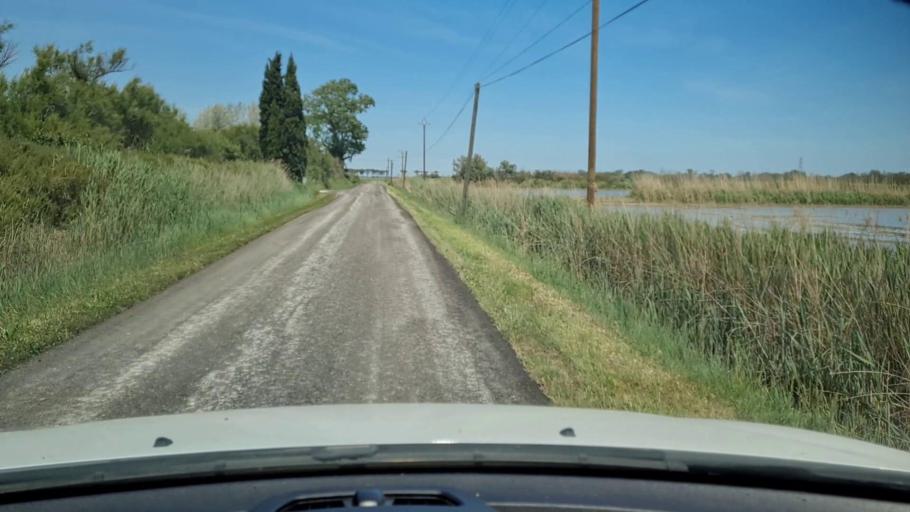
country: FR
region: Languedoc-Roussillon
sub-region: Departement du Gard
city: Saint-Gilles
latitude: 43.5670
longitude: 4.3923
